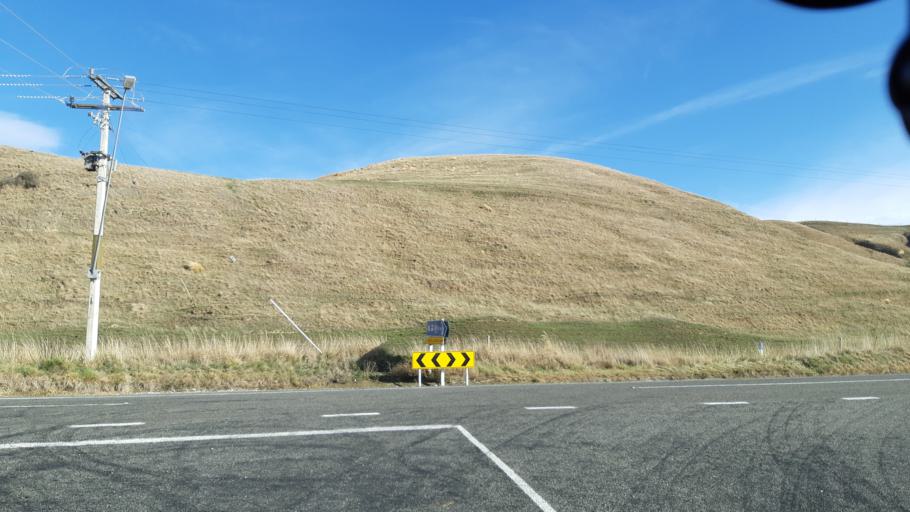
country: NZ
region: Marlborough
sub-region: Marlborough District
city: Blenheim
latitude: -41.7470
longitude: 174.1375
